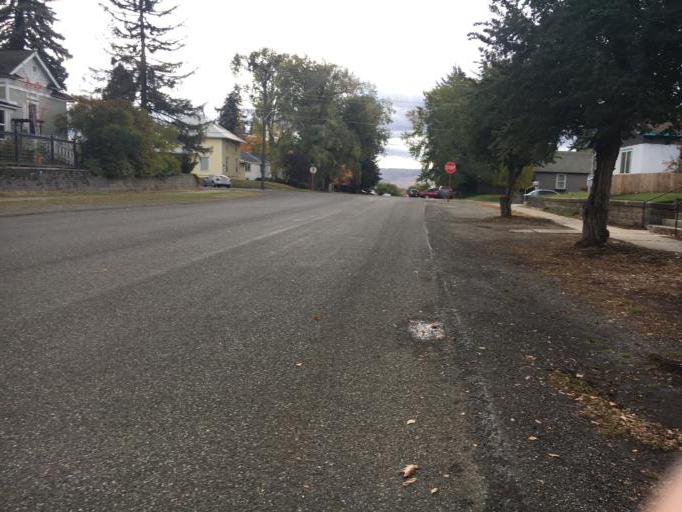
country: US
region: Washington
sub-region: Kittitas County
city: Ellensburg
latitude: 46.9980
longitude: -120.5515
